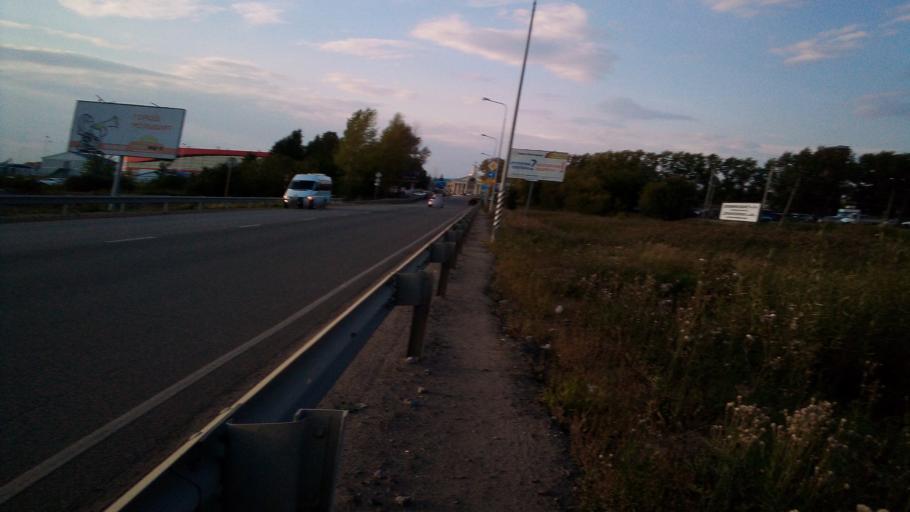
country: RU
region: Chelyabinsk
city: Potanino
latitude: 55.2932
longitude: 61.5115
